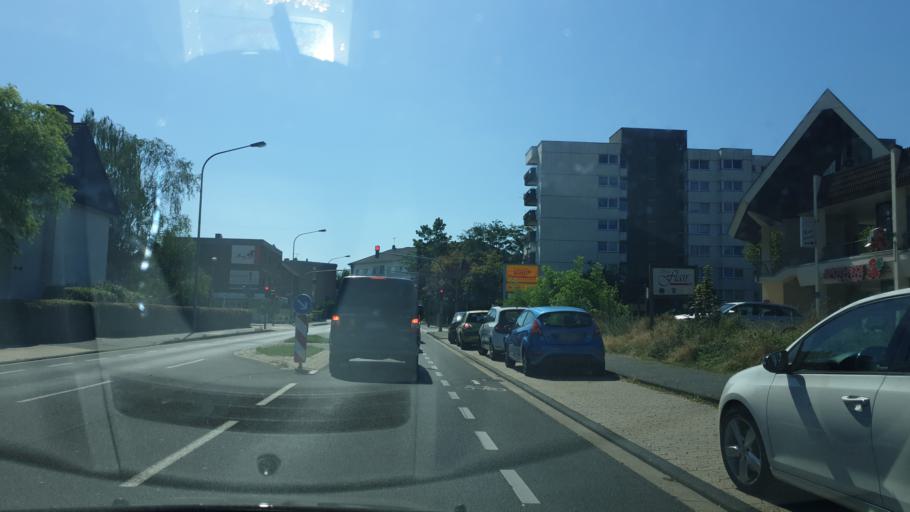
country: DE
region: North Rhine-Westphalia
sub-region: Regierungsbezirk Koln
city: Euskirchen
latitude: 50.6645
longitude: 6.7745
